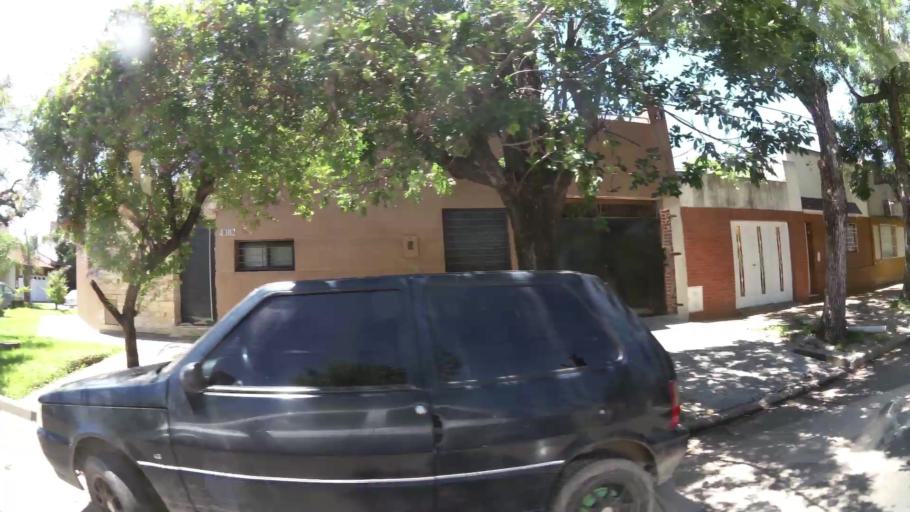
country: AR
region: Santa Fe
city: Santa Fe de la Vera Cruz
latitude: -31.6255
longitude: -60.7114
